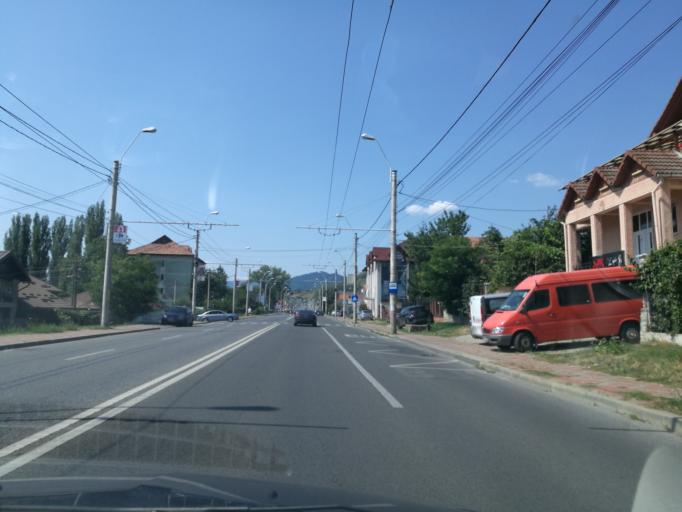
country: RO
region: Neamt
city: Piatra Neamt
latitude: 46.9376
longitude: 26.3440
